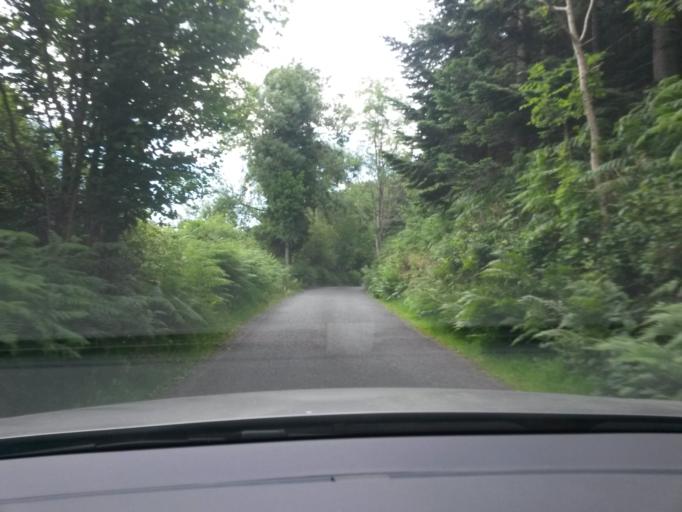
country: IE
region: Leinster
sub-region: Wicklow
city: Enniskerry
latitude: 53.1708
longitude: -6.2399
